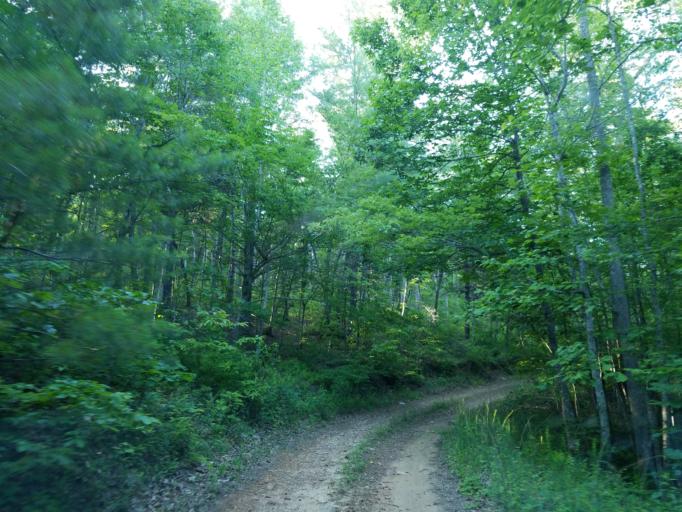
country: US
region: Georgia
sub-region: Fannin County
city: Blue Ridge
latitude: 34.8151
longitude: -84.1584
